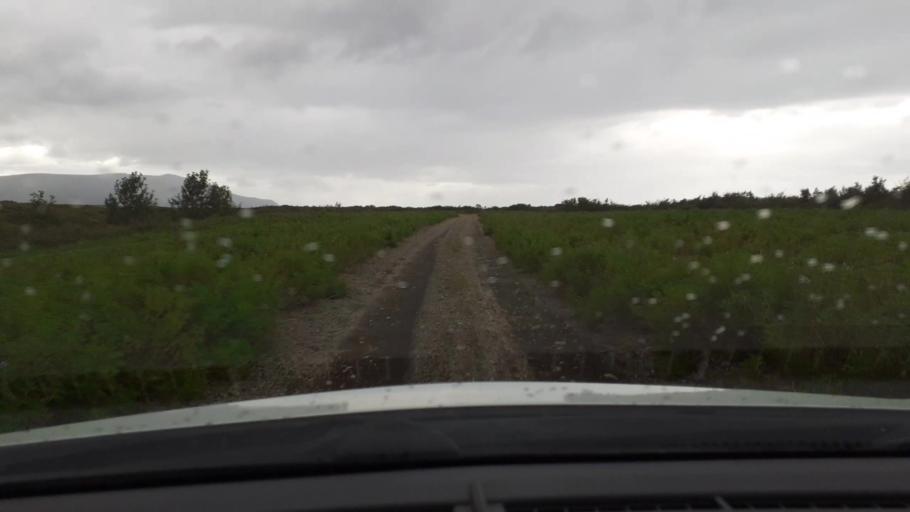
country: IS
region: West
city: Borgarnes
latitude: 64.4577
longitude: -21.9509
